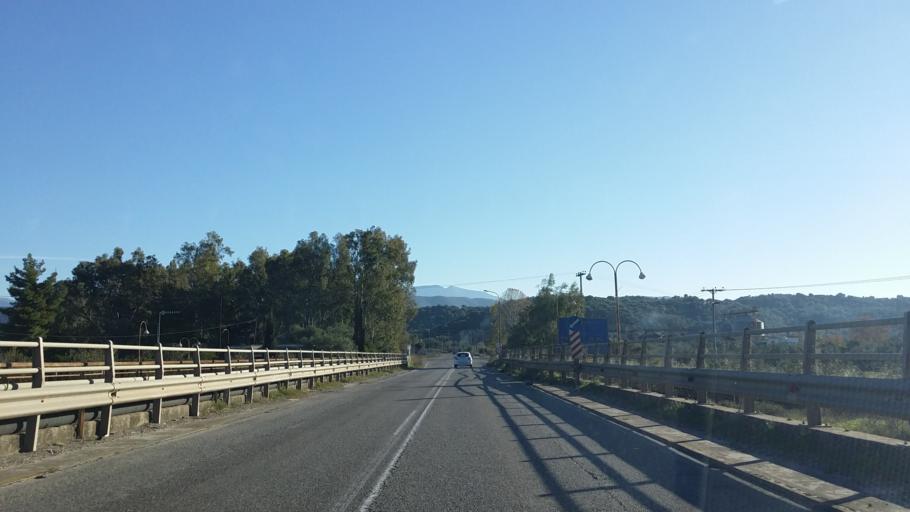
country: GR
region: West Greece
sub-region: Nomos Aitolias kai Akarnanias
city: Neapolis
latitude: 38.6699
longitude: 21.3398
